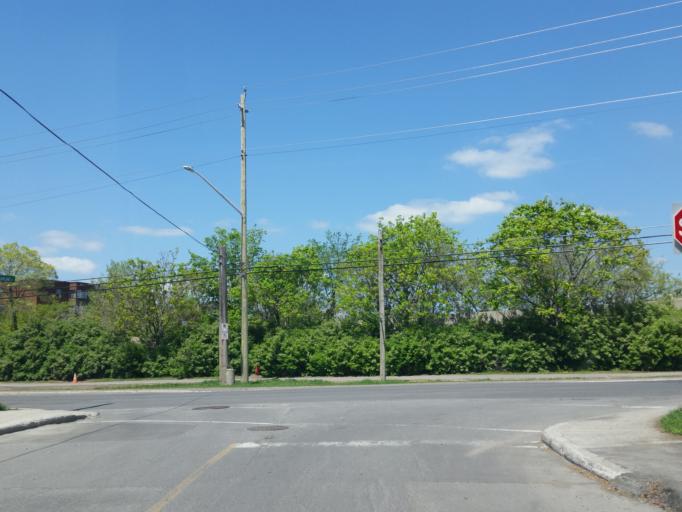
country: CA
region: Ontario
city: Ottawa
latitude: 45.4072
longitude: -75.7256
